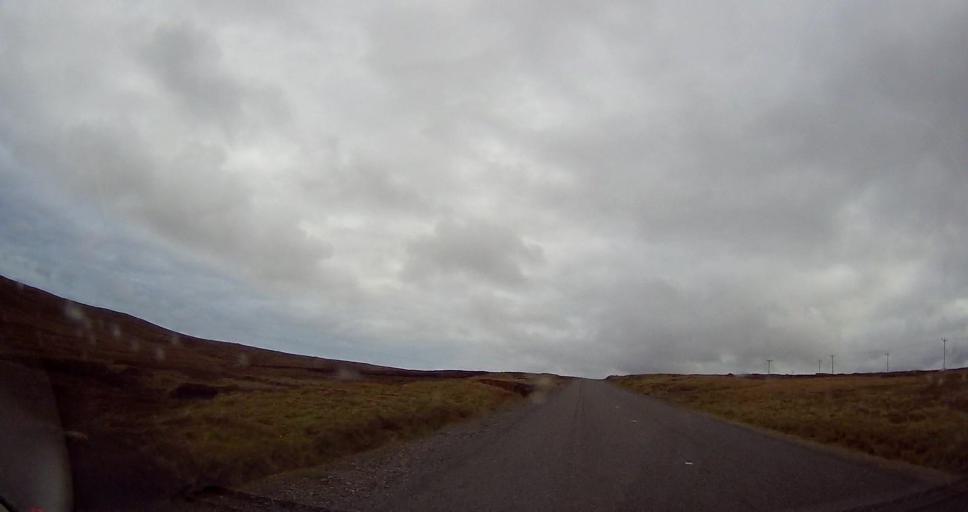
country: GB
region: Scotland
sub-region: Shetland Islands
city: Shetland
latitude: 60.6216
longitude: -1.0744
